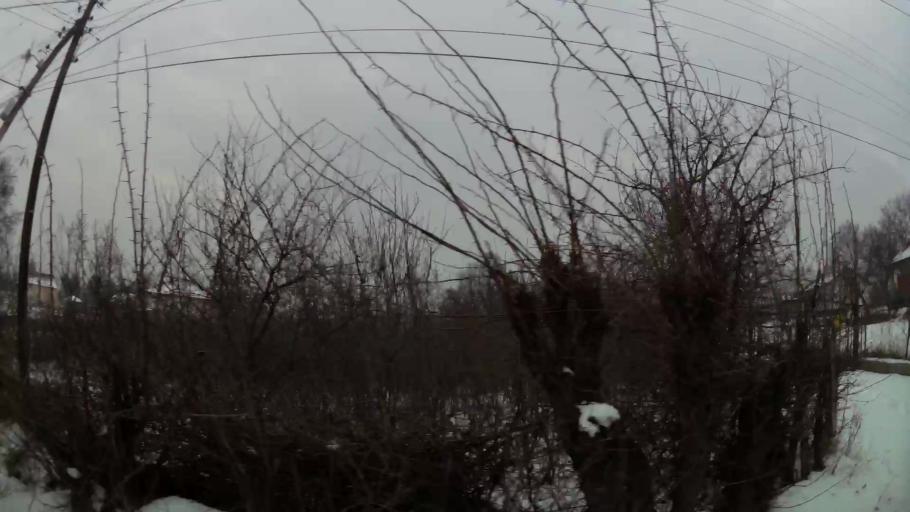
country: MK
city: Kondovo
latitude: 42.0312
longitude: 21.3414
